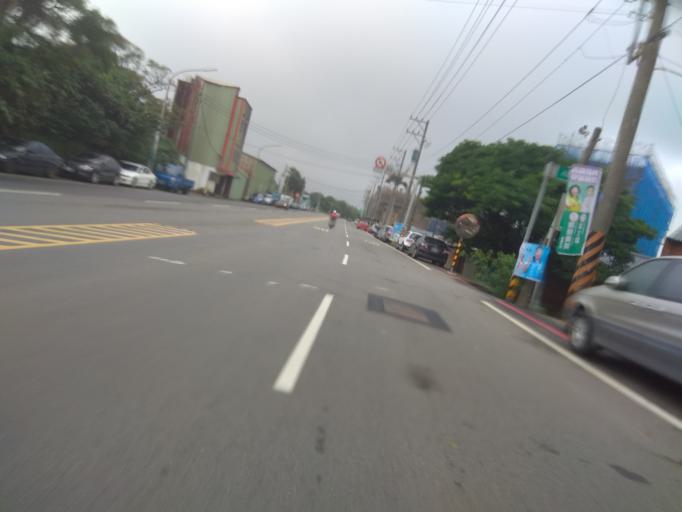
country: TW
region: Taiwan
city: Taoyuan City
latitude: 25.0318
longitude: 121.1012
